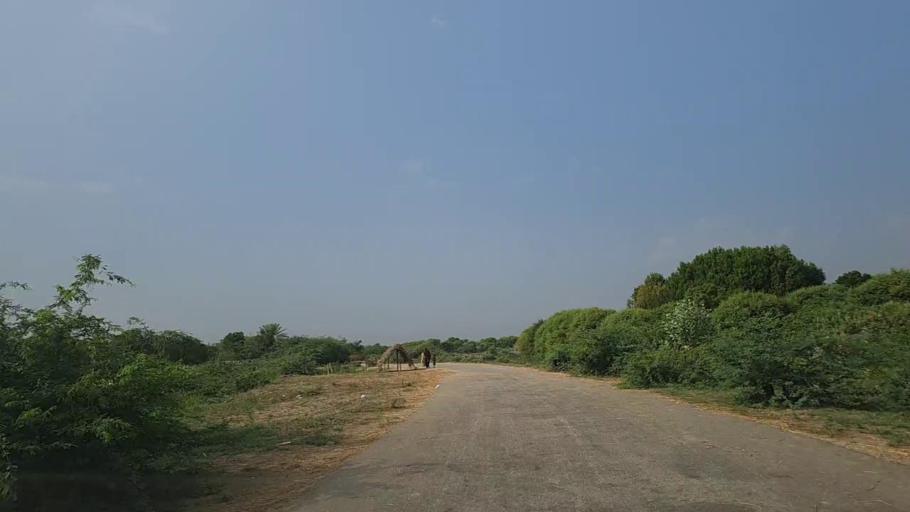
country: PK
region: Sindh
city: Daro Mehar
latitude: 24.7193
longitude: 68.1582
